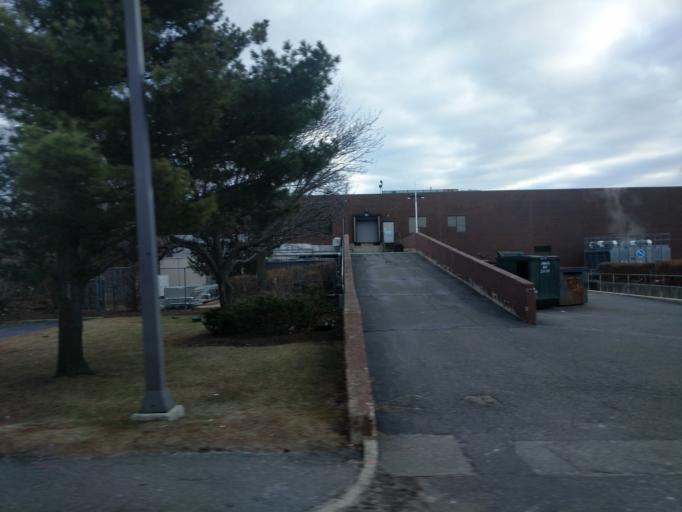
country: US
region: New York
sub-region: Nassau County
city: East Garden City
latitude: 40.7232
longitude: -73.6047
